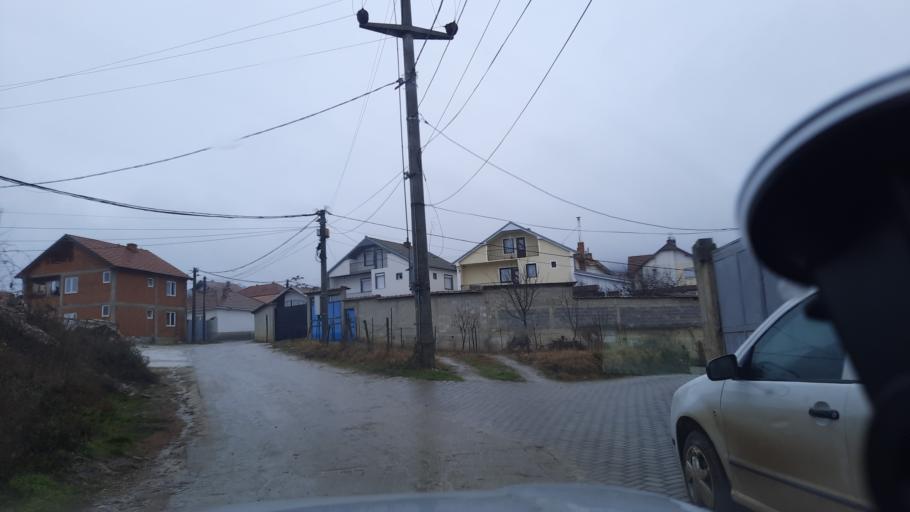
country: MK
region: Opstina Lipkovo
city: Matejche
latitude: 42.1240
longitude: 21.5935
